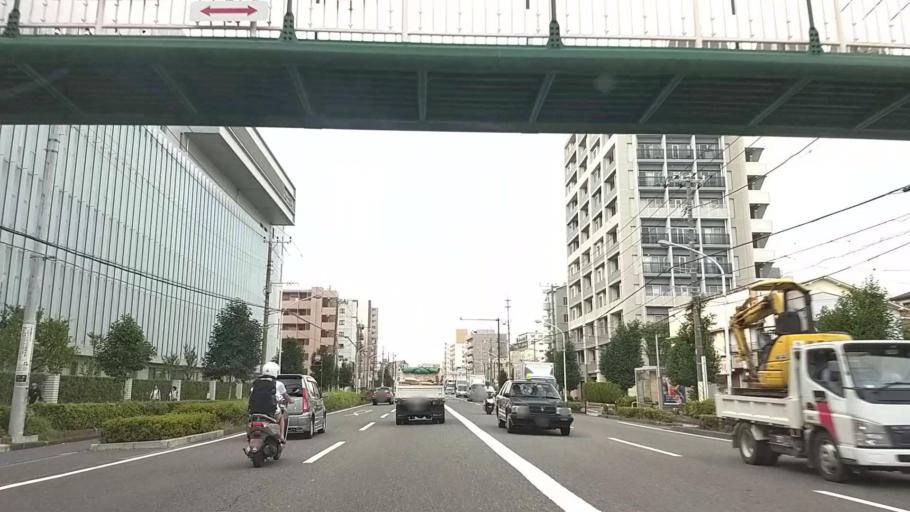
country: JP
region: Kanagawa
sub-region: Kawasaki-shi
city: Kawasaki
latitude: 35.5275
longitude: 139.7138
